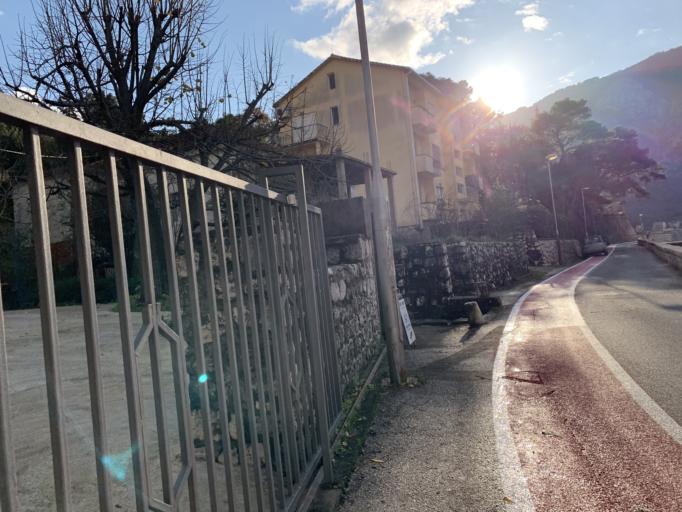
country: ME
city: Dobrota
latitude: 42.4430
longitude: 18.7637
